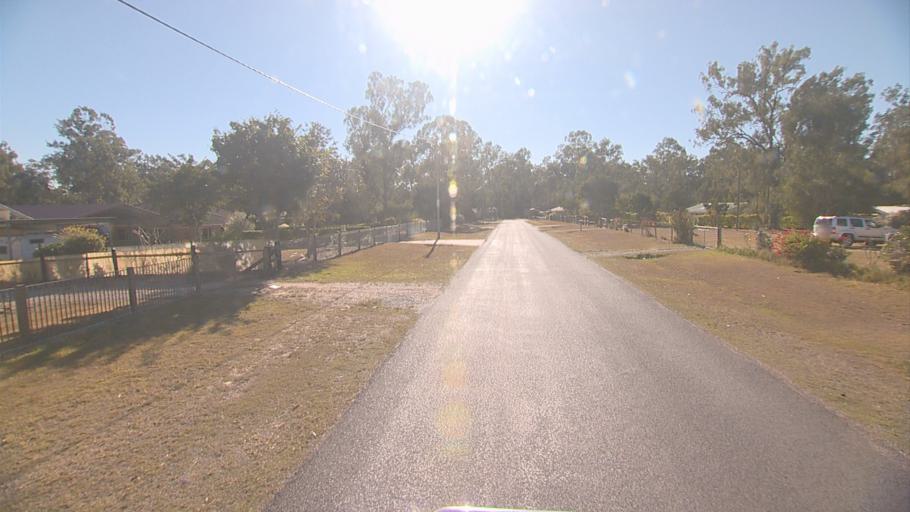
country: AU
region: Queensland
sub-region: Logan
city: North Maclean
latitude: -27.8047
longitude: 152.9862
